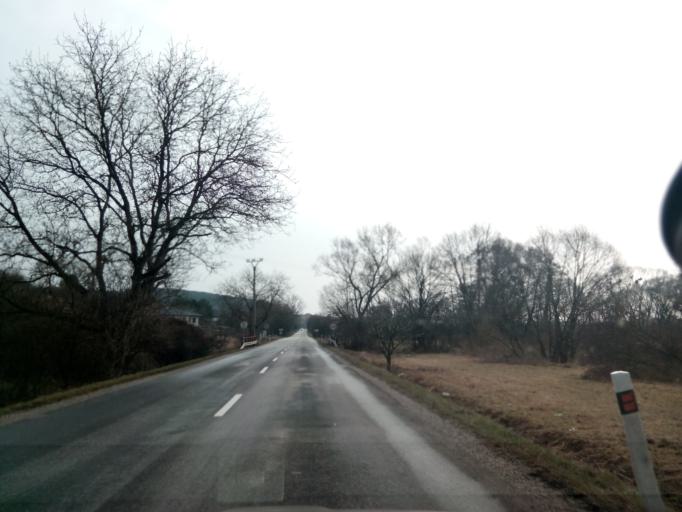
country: SK
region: Kosicky
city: Secovce
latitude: 48.6319
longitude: 21.5162
